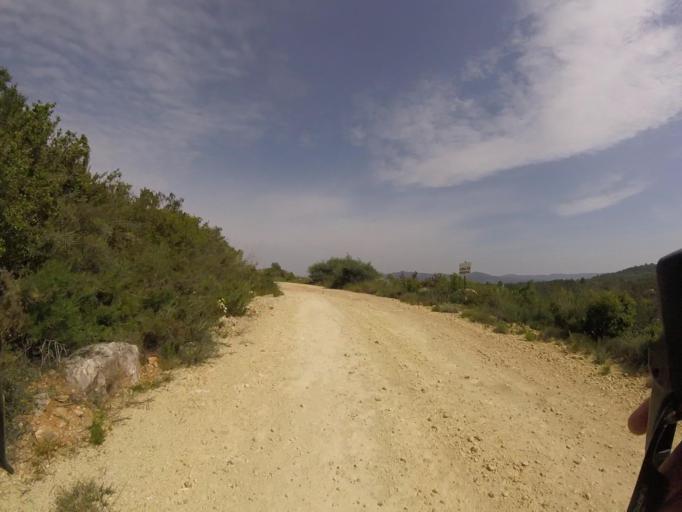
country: ES
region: Valencia
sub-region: Provincia de Castello
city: Cuevas de Vinroma
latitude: 40.2902
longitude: 0.1210
